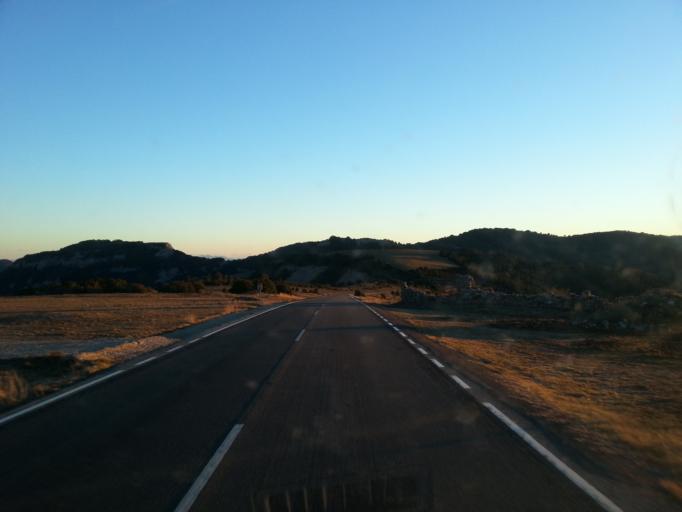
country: ES
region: Catalonia
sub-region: Provincia de Lleida
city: Olius
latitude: 42.1229
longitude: 1.5441
